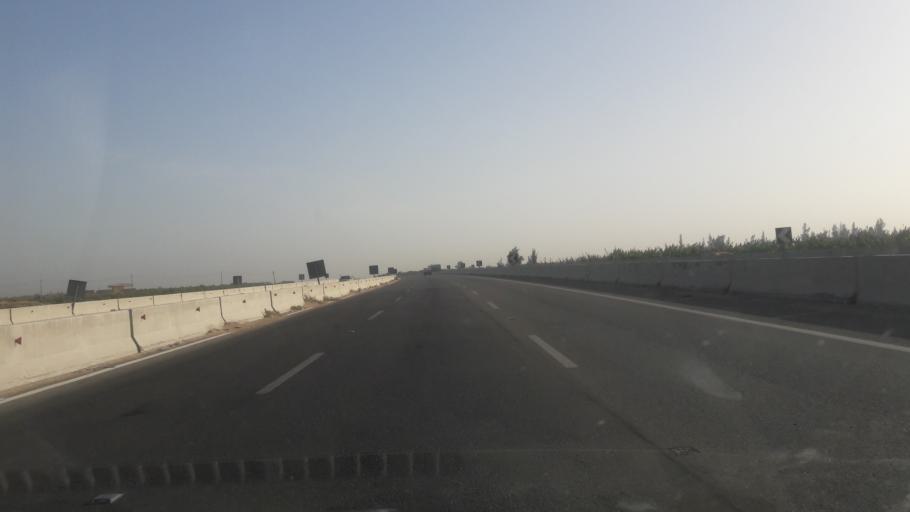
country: EG
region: Al Isma'iliyah
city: Ismailia
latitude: 30.6418
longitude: 32.0923
